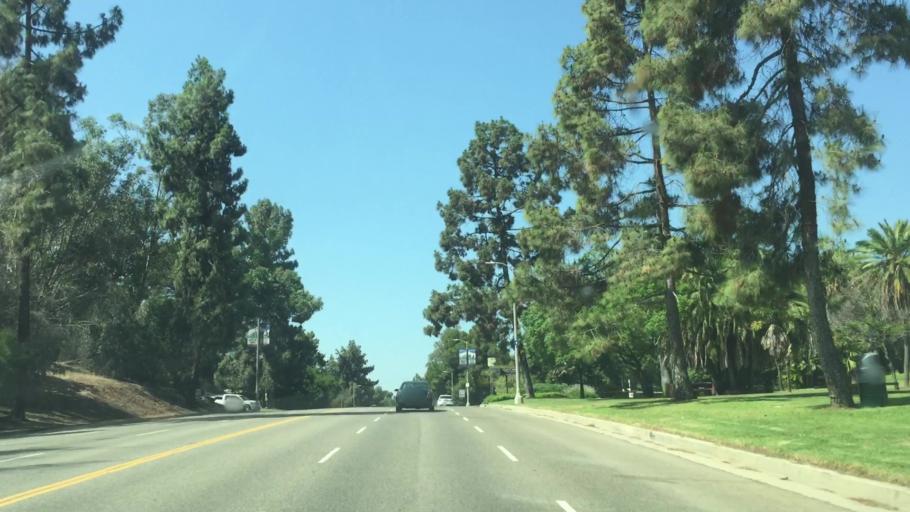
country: US
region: California
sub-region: Los Angeles County
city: Echo Park
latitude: 34.0866
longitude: -118.2425
